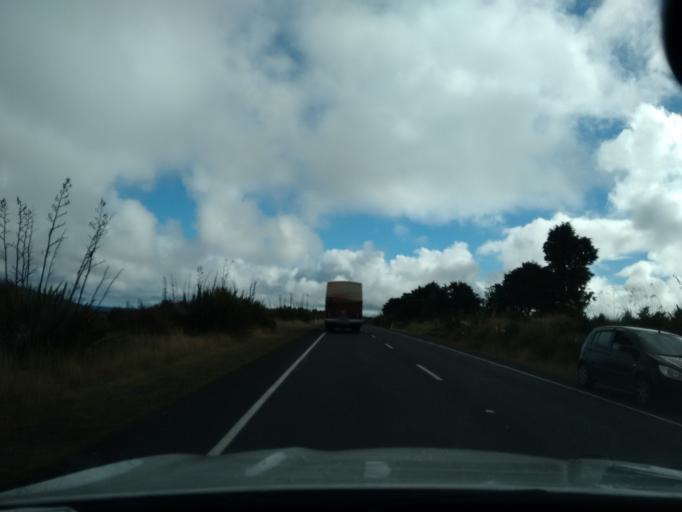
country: NZ
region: Manawatu-Wanganui
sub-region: Ruapehu District
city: Waiouru
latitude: -39.1833
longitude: 175.4397
